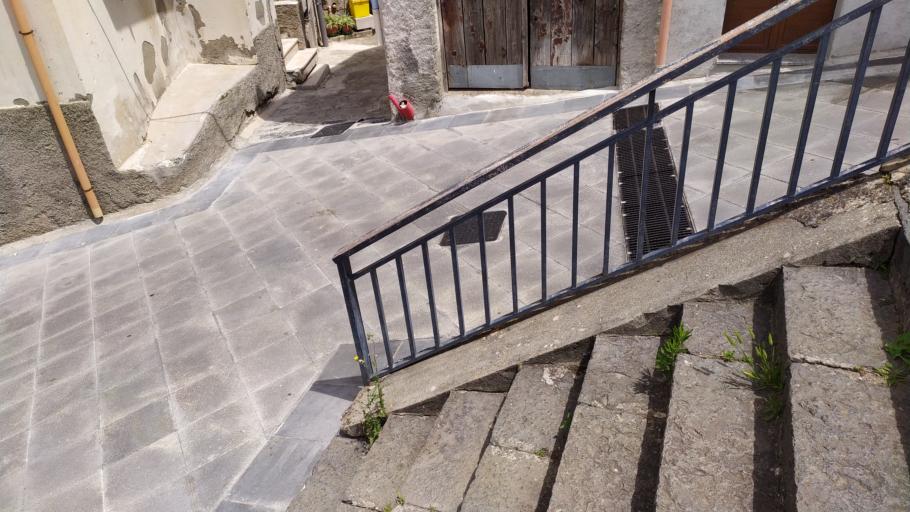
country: IT
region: Sicily
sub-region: Messina
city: San Pier Niceto
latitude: 38.1594
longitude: 15.3502
